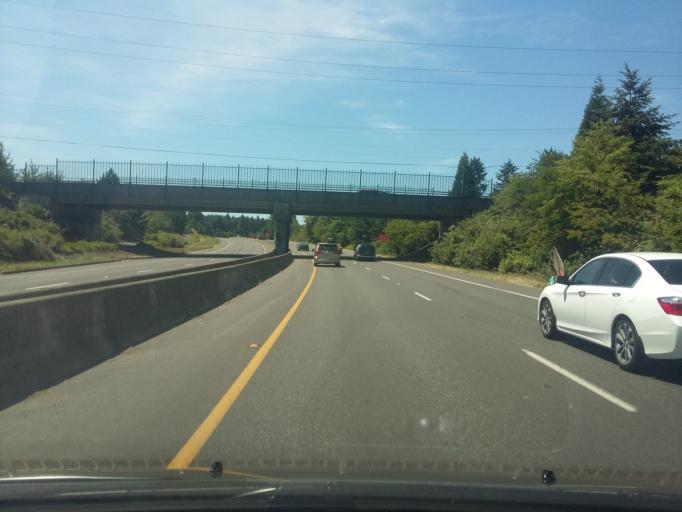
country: US
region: Washington
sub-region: Clark County
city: Five Corners
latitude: 45.6823
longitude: -122.5622
